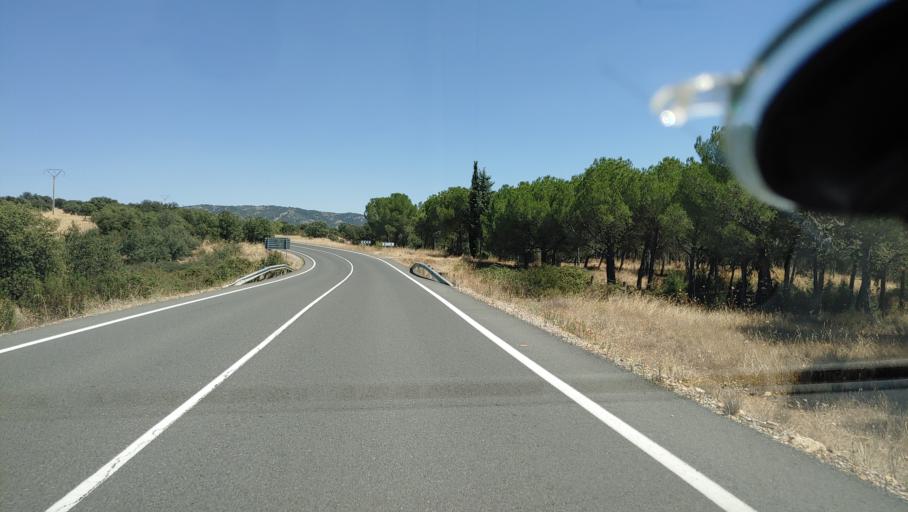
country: ES
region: Castille-La Mancha
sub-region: Provincia de Ciudad Real
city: Almaden
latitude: 38.8314
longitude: -4.7051
